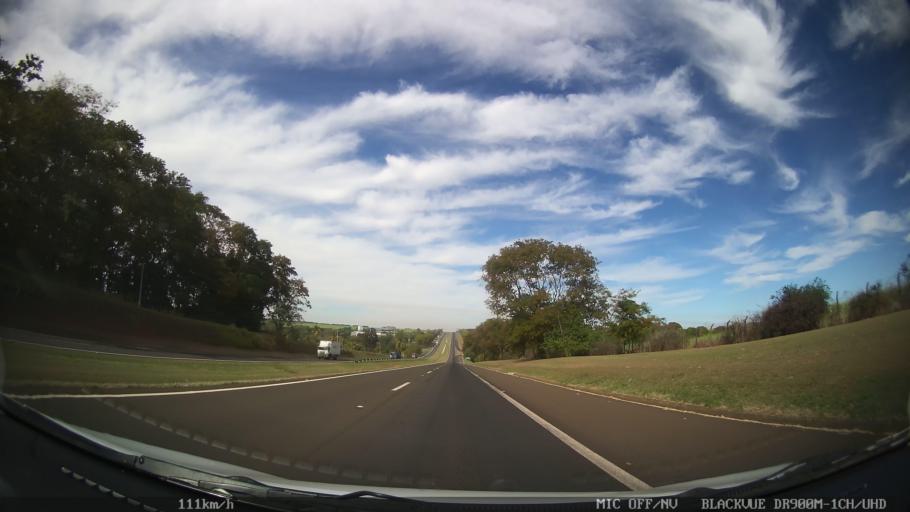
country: BR
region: Sao Paulo
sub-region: Matao
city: Matao
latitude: -21.6605
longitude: -48.3741
